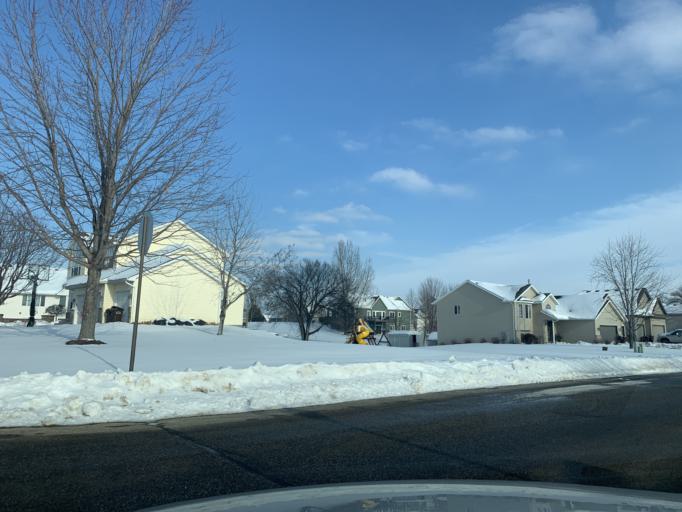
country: US
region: Minnesota
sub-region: Wright County
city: Buffalo
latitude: 45.2010
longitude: -93.8341
